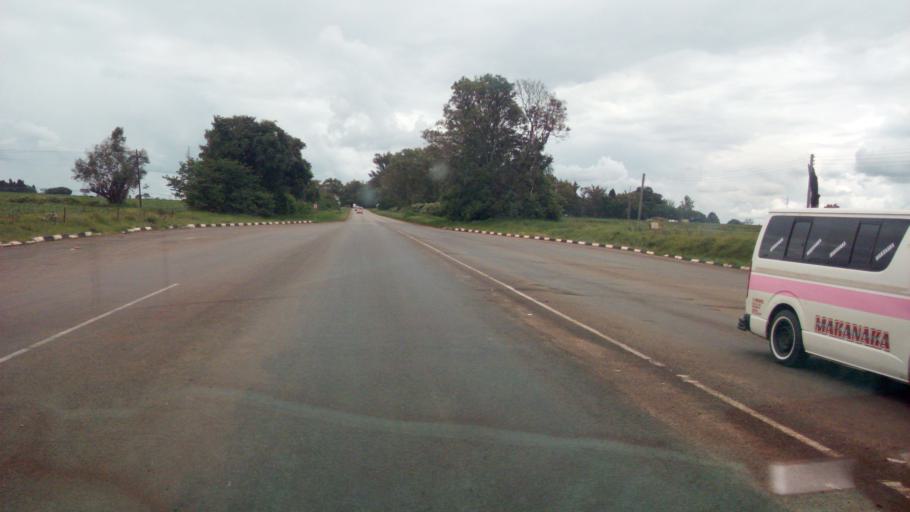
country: ZW
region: Harare
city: Harare
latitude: -17.6912
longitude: 31.0076
